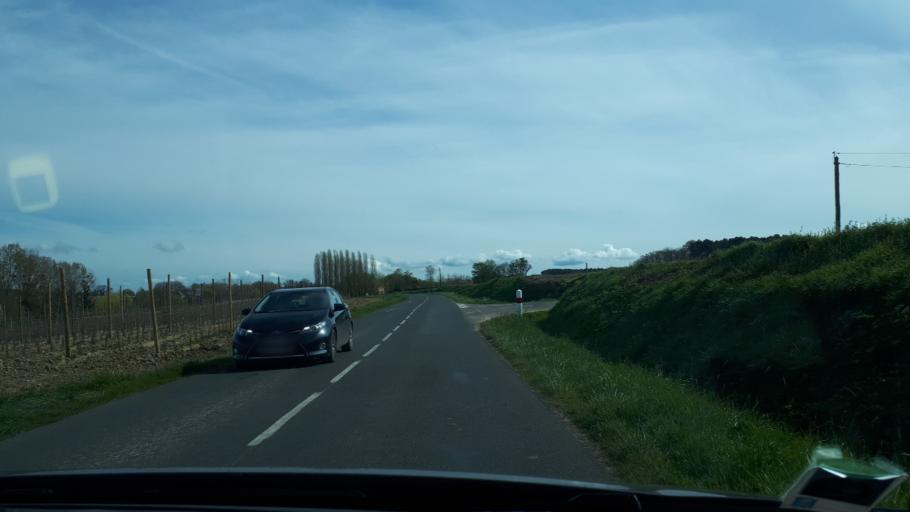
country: FR
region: Pays de la Loire
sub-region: Departement de la Sarthe
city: Cerans-Foulletourte
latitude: 47.8098
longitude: 0.1139
